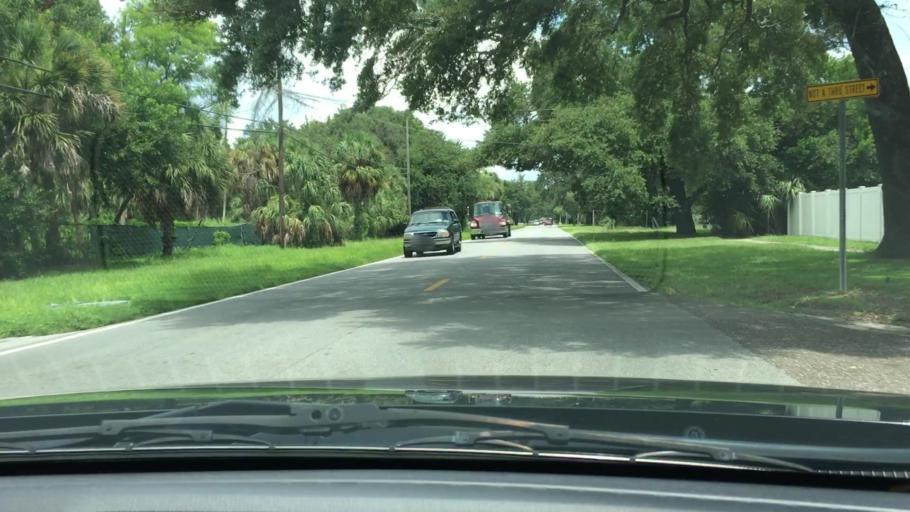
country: US
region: Florida
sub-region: Hillsborough County
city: Tampa
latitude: 27.8983
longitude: -82.5267
